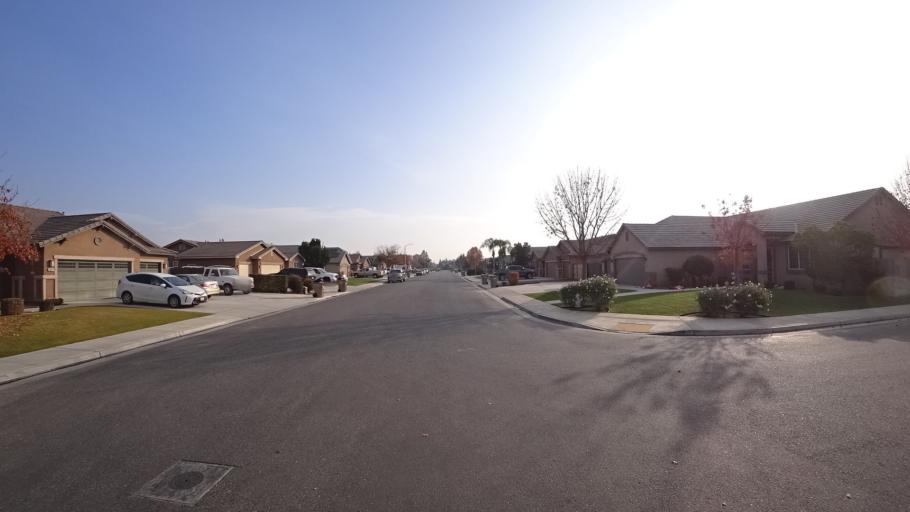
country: US
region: California
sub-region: Kern County
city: Greenacres
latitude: 35.4366
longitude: -119.1145
